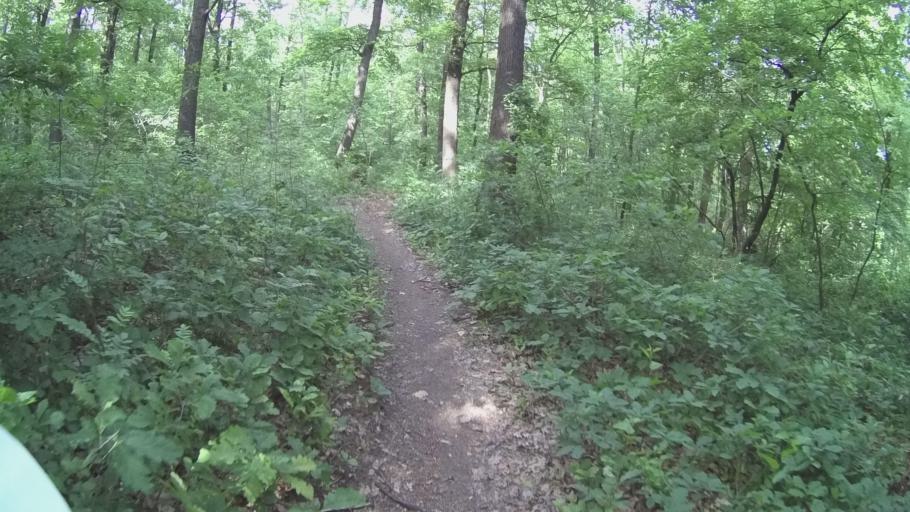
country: CZ
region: Central Bohemia
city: Zdiby
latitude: 50.2035
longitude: 14.4469
